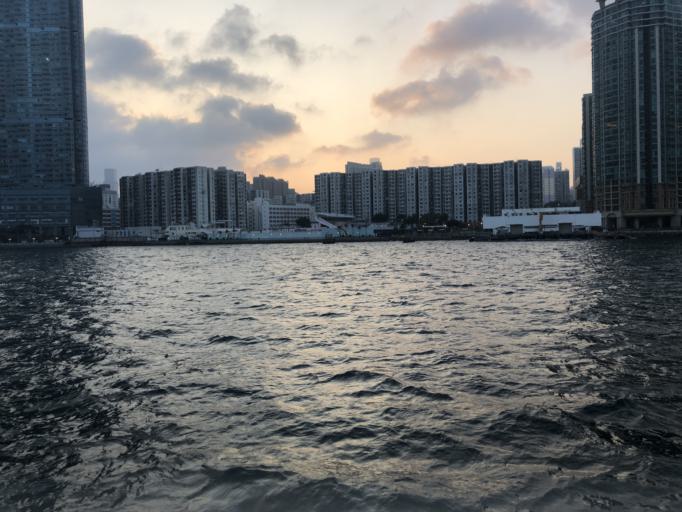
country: HK
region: Kowloon City
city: Kowloon
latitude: 22.3057
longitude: 114.1959
